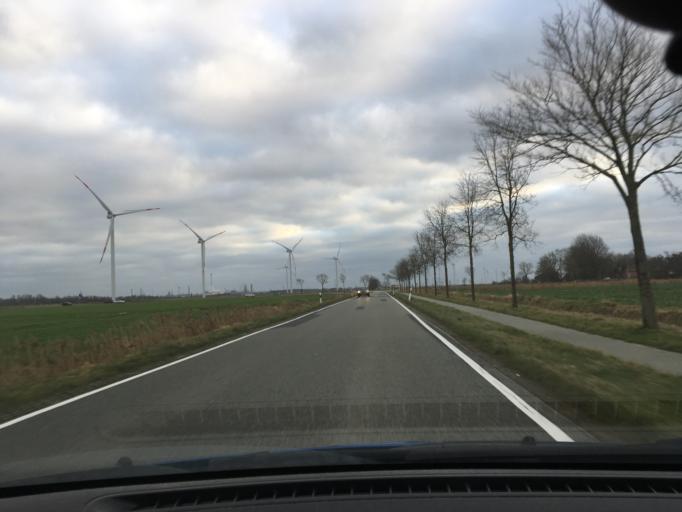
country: DE
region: Schleswig-Holstein
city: Norderwohrden
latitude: 54.1905
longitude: 9.0373
